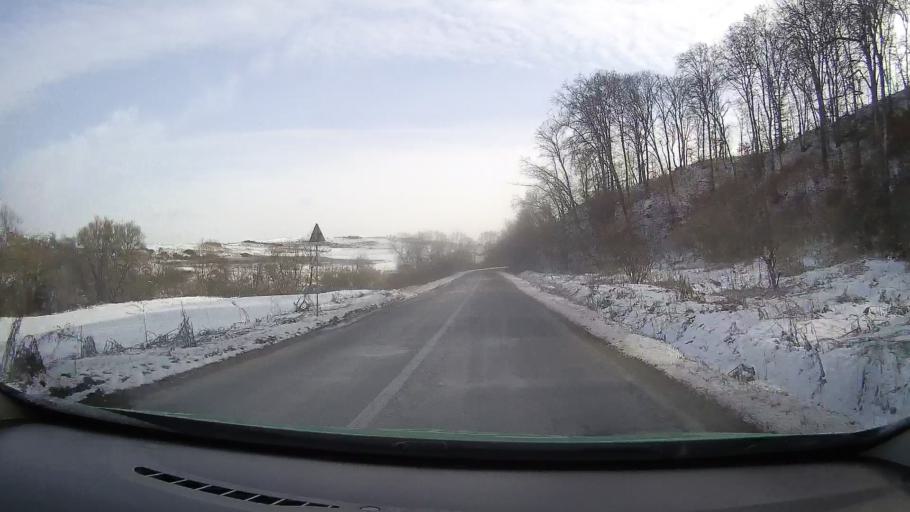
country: RO
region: Mures
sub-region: Comuna Apold
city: Saes
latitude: 46.1709
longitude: 24.7570
